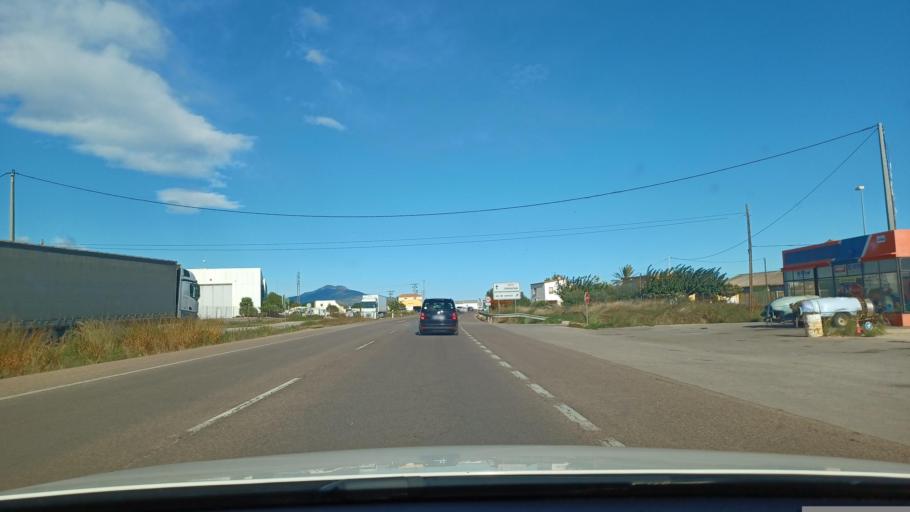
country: ES
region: Valencia
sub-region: Provincia de Castello
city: Vinaros
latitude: 40.4745
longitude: 0.4668
